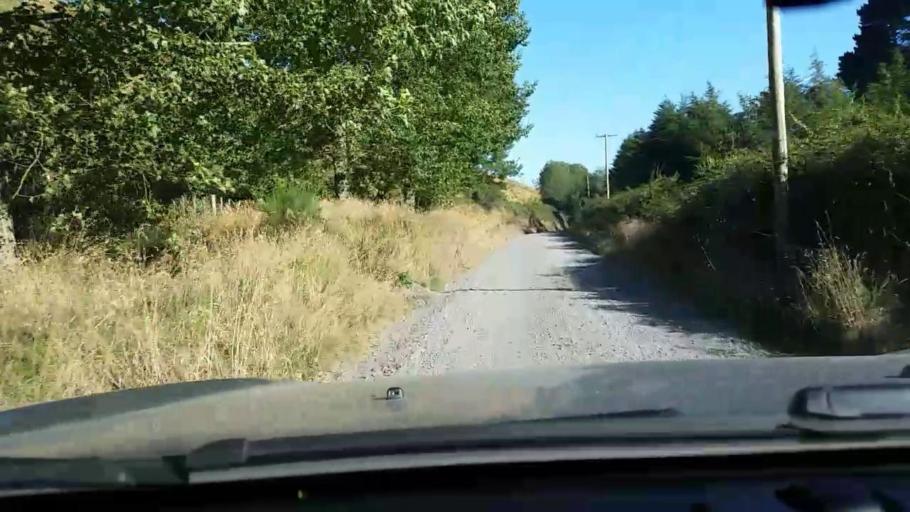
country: NZ
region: Bay of Plenty
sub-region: Rotorua District
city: Rotorua
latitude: -38.3940
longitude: 176.1728
